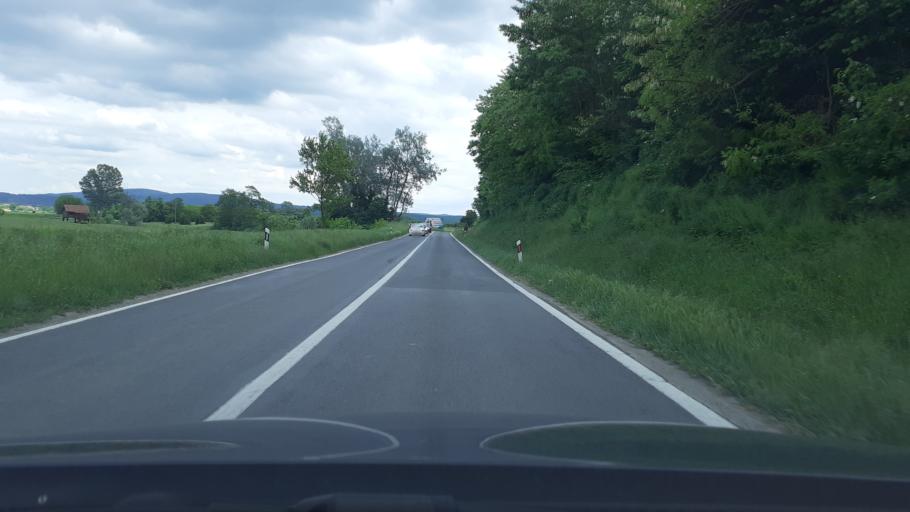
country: HR
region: Pozesko-Slavonska
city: Gradac
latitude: 45.3123
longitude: 17.7806
